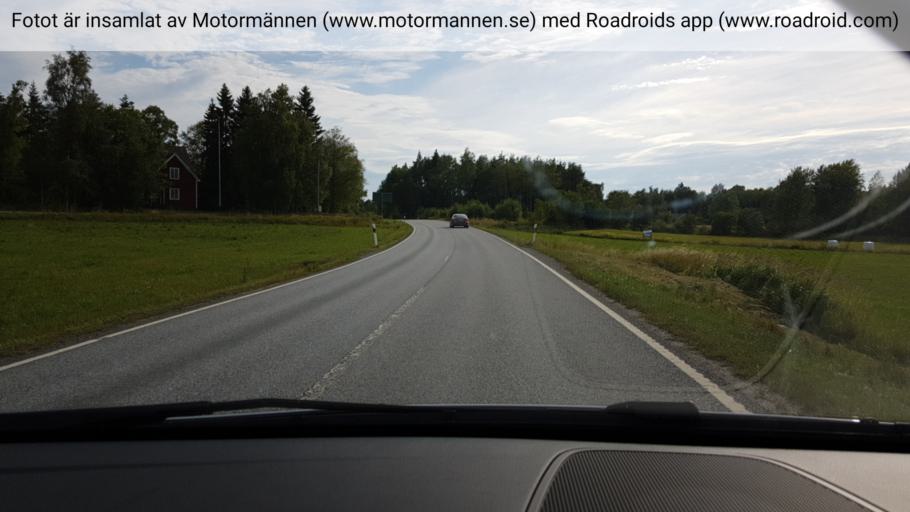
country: SE
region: Stockholm
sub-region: Norrtalje Kommun
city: Hallstavik
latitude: 59.9510
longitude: 18.7623
